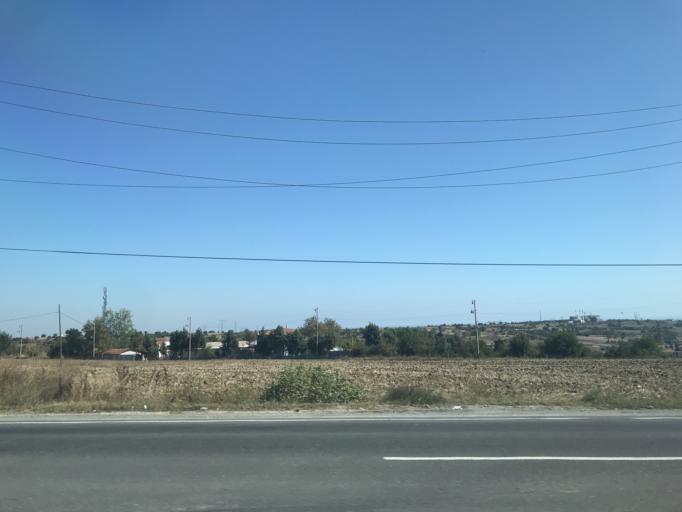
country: TR
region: Tekirdag
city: Tekirdag
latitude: 41.0013
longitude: 27.5104
